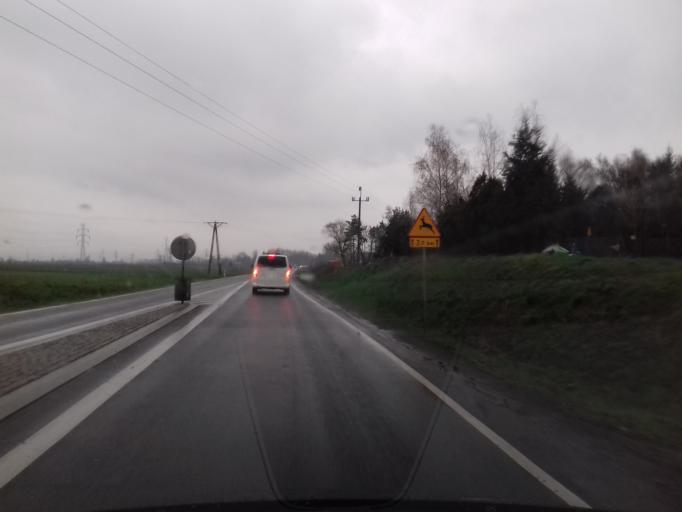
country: PL
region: Lesser Poland Voivodeship
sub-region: Powiat nowosadecki
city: Stary Sacz
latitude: 49.5521
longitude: 20.6547
